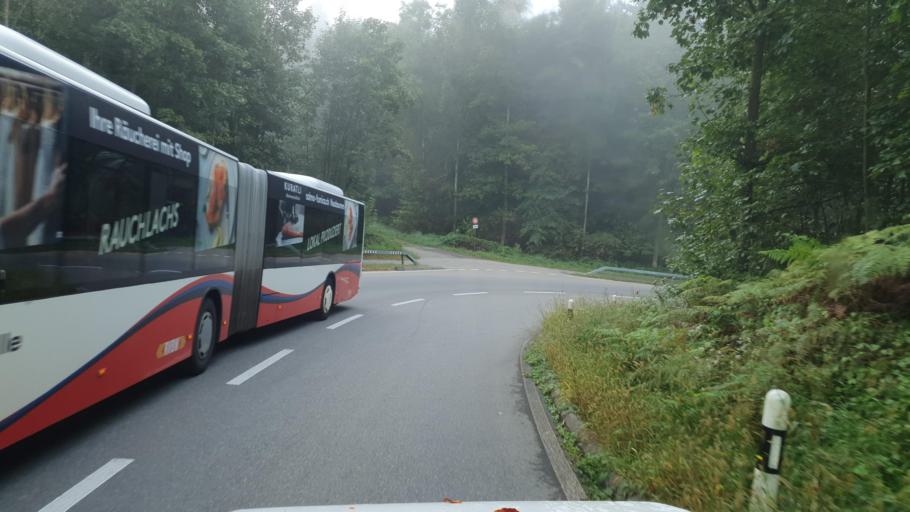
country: CH
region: Aargau
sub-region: Bezirk Baden
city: Mellingen
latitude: 47.4465
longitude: 8.2838
